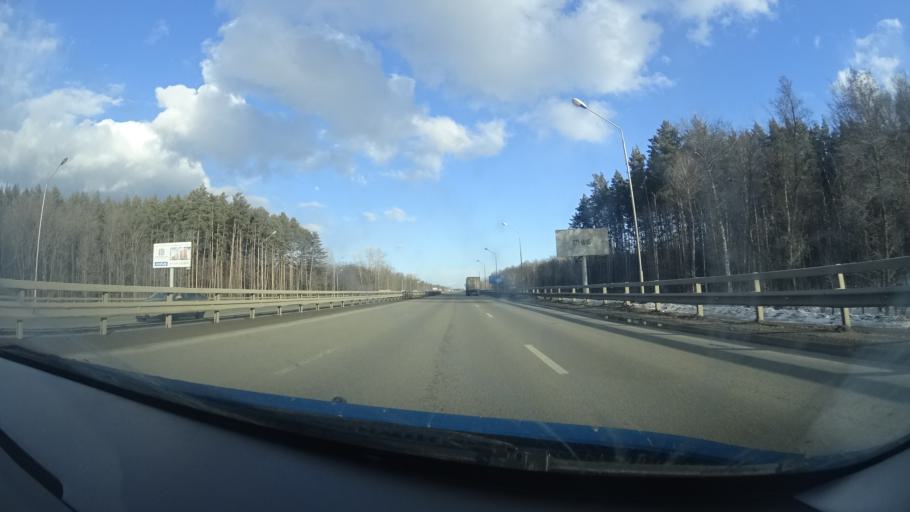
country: RU
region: Bashkortostan
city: Avdon
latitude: 54.6710
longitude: 55.8346
